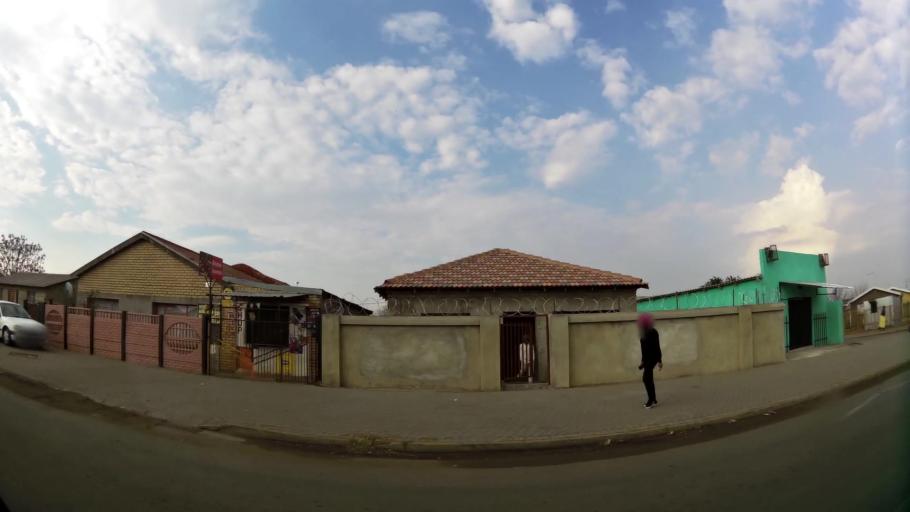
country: ZA
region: Gauteng
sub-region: Sedibeng District Municipality
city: Vanderbijlpark
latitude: -26.6967
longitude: 27.8662
